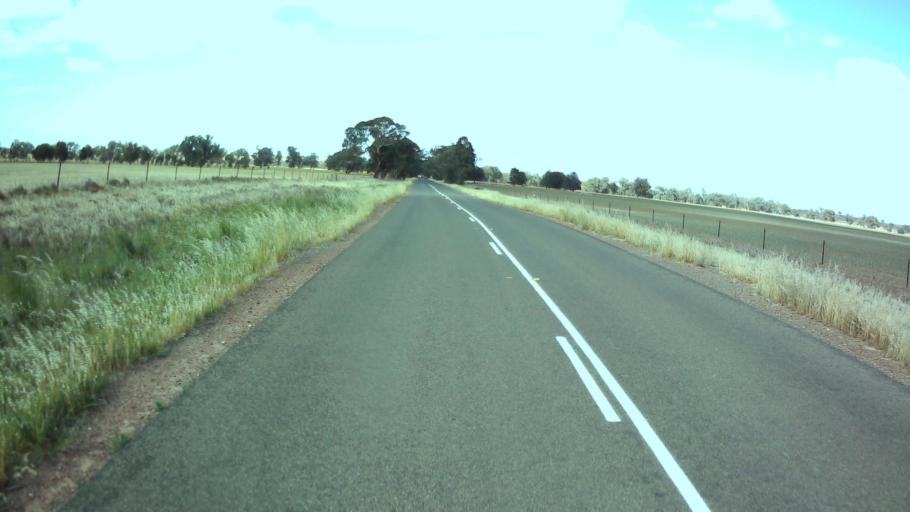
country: AU
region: New South Wales
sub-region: Weddin
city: Grenfell
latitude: -33.9794
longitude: 148.4197
